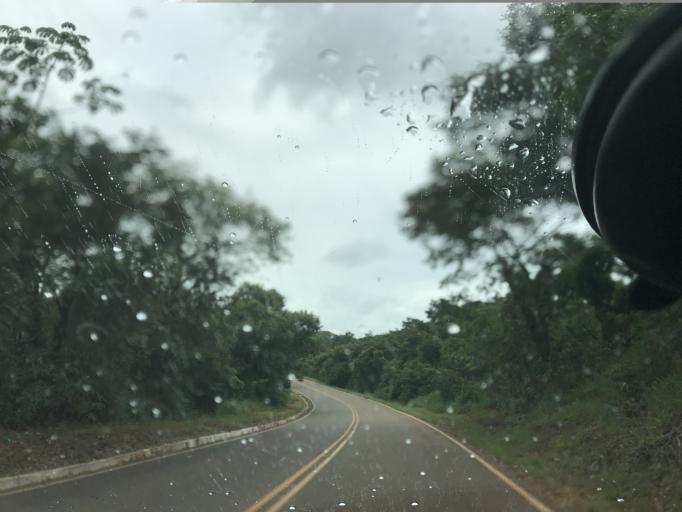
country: BR
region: Minas Gerais
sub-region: Conceicao Do Rio Verde
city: Conceicao do Rio Verde
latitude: -21.6854
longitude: -45.0161
